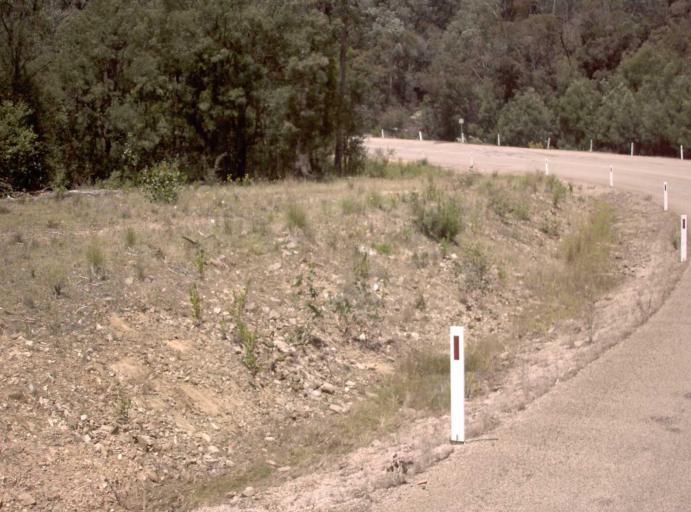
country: AU
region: Victoria
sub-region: East Gippsland
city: Lakes Entrance
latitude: -37.5671
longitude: 147.8882
